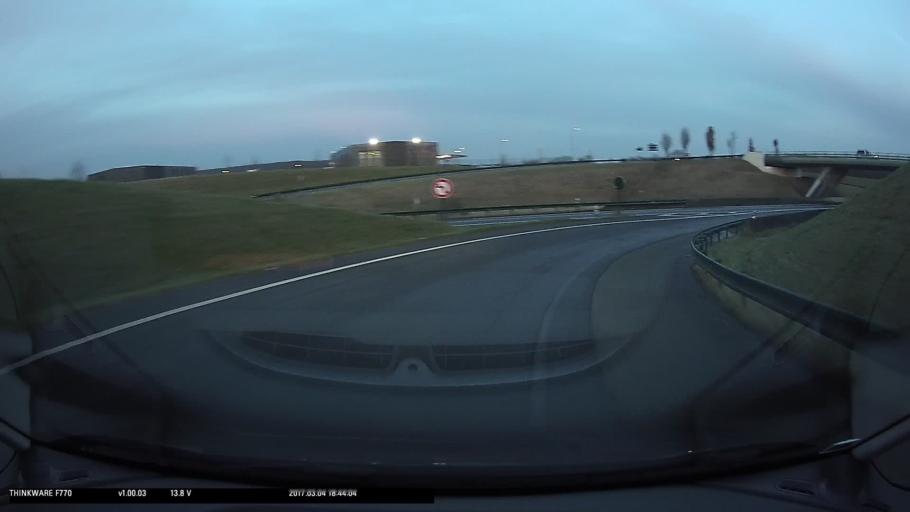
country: FR
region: Ile-de-France
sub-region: Departement du Val-d'Oise
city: Marines
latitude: 49.1413
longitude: 1.9651
